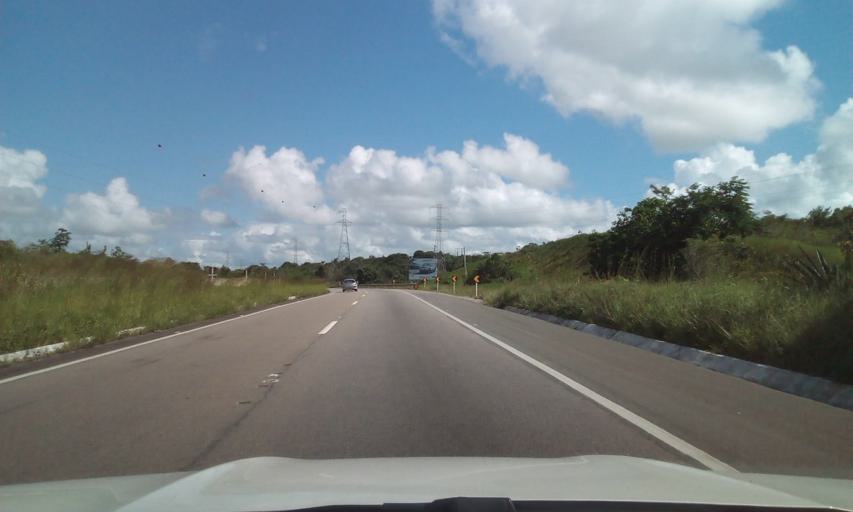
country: BR
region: Paraiba
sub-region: Conde
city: Conde
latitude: -7.3123
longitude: -34.9459
